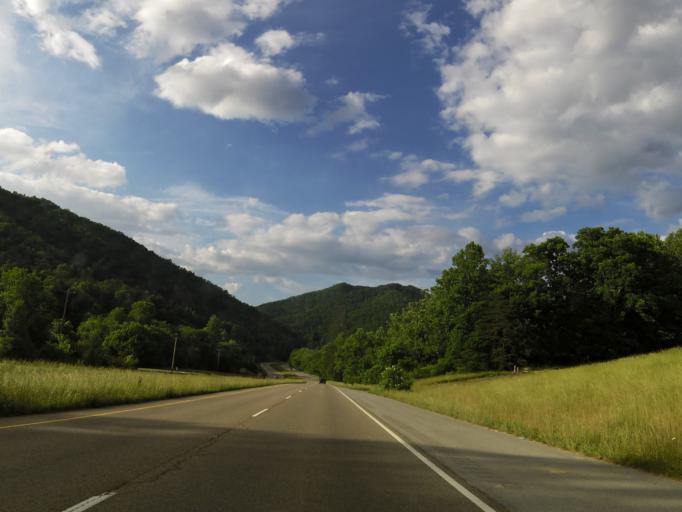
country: US
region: Tennessee
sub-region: Blount County
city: Wildwood
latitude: 35.7207
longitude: -83.8192
